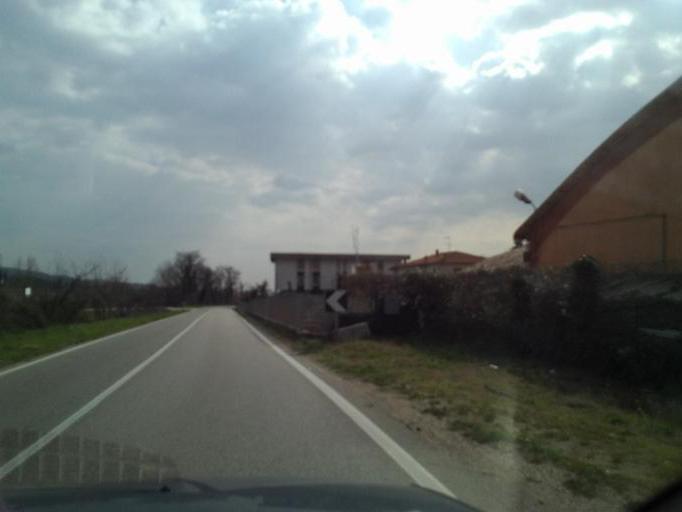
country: IT
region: Veneto
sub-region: Provincia di Verona
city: Negrar
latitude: 45.5428
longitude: 10.9427
